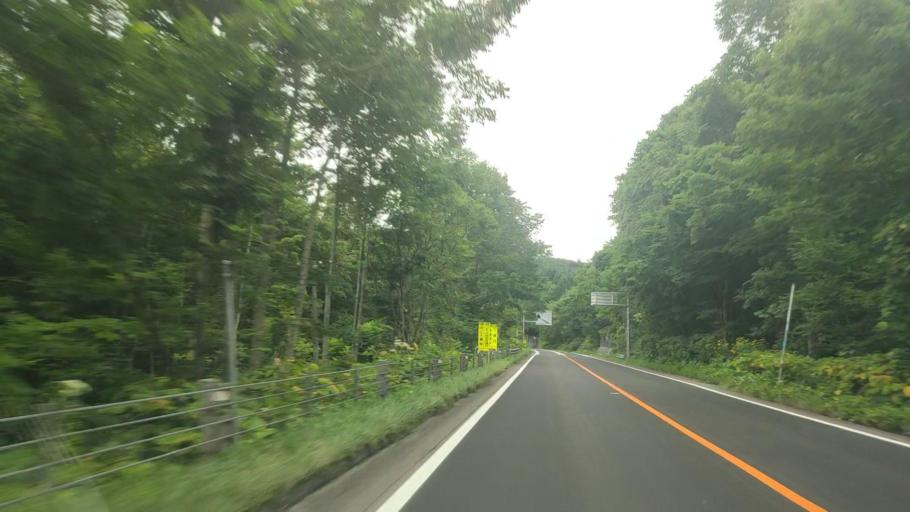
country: JP
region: Hokkaido
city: Niseko Town
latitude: 42.5975
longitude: 140.6040
